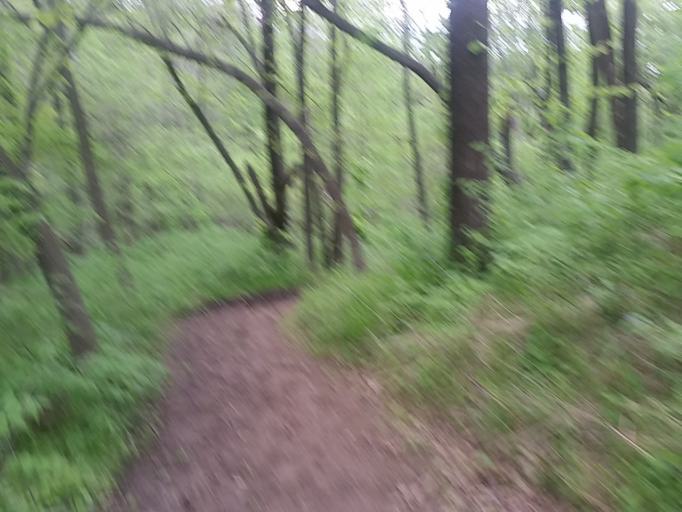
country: US
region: Nebraska
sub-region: Sarpy County
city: Bellevue
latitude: 41.1778
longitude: -95.9089
